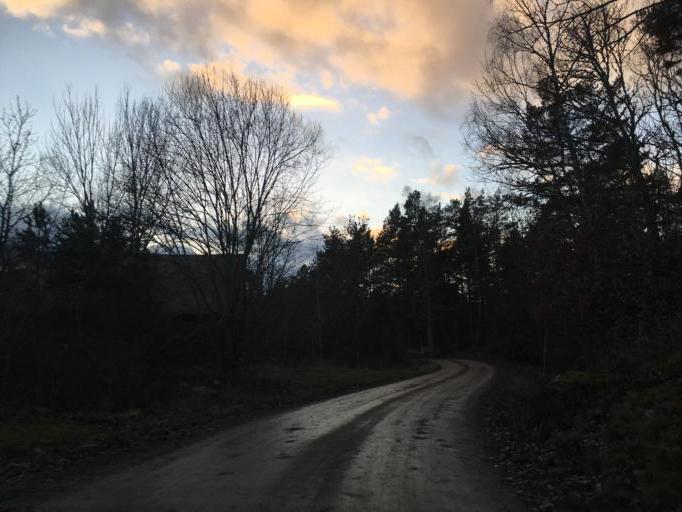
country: SE
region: Kalmar
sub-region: Vasterviks Kommun
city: Vaestervik
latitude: 57.6034
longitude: 16.5316
